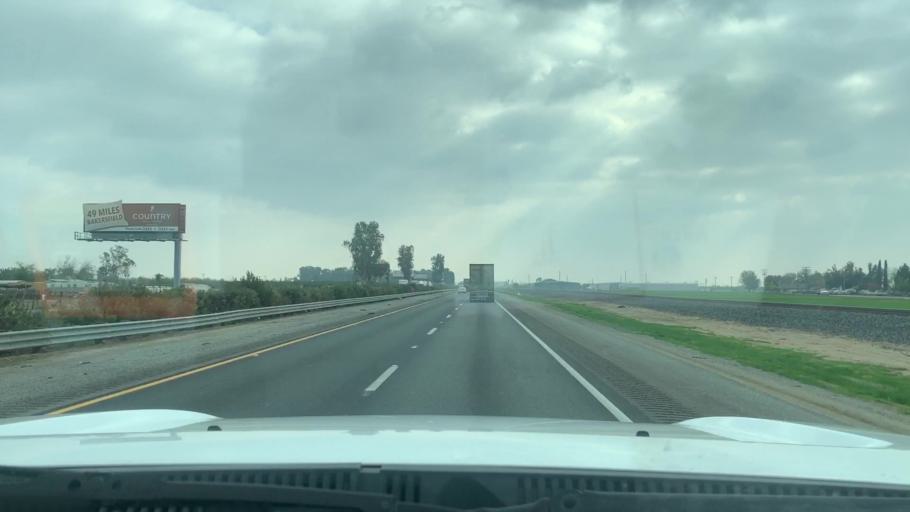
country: US
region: California
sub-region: Tulare County
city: Pixley
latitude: 35.9901
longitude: -119.2987
